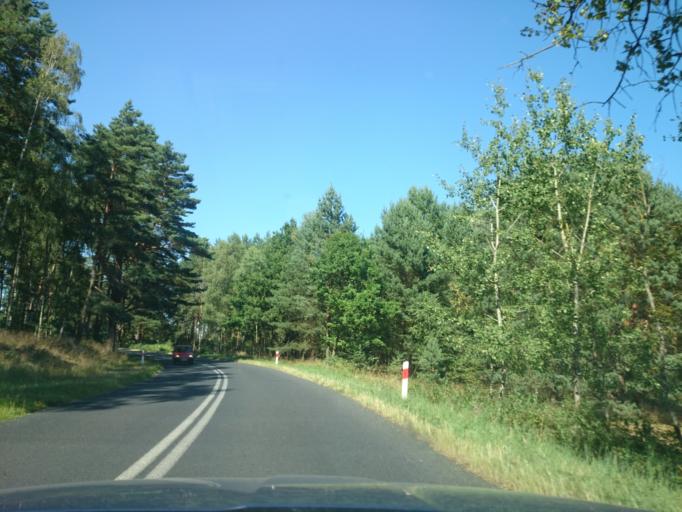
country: PL
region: West Pomeranian Voivodeship
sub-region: Powiat policki
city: Nowe Warpno
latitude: 53.6863
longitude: 14.3560
